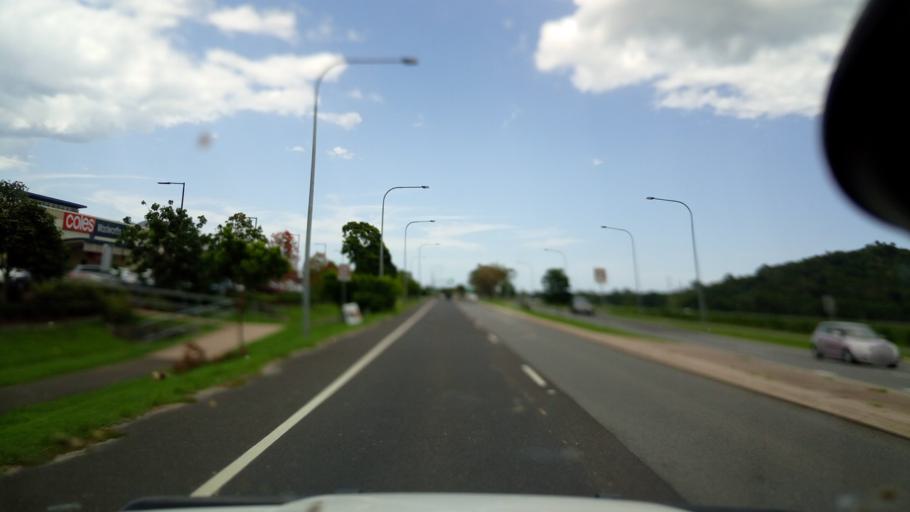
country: AU
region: Queensland
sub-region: Cairns
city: Redlynch
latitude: -16.8974
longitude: 145.6999
